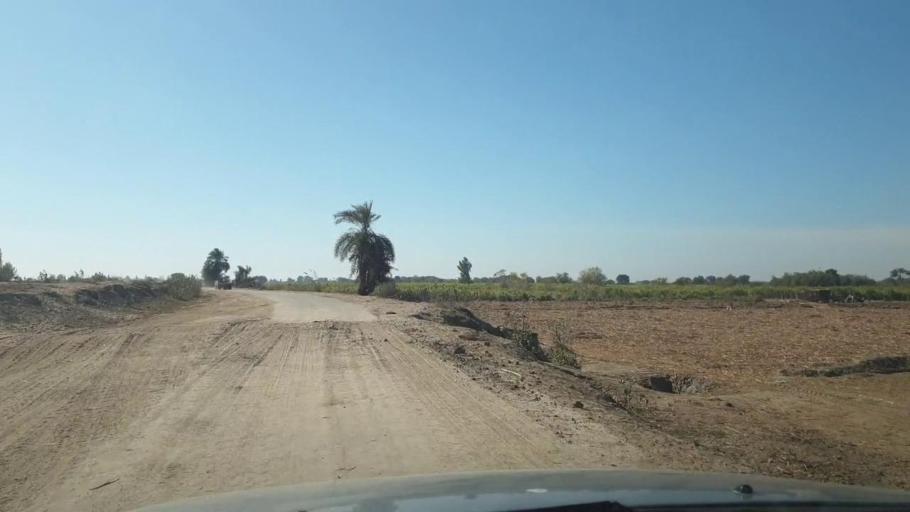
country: PK
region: Sindh
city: Ghotki
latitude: 28.0231
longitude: 69.2688
